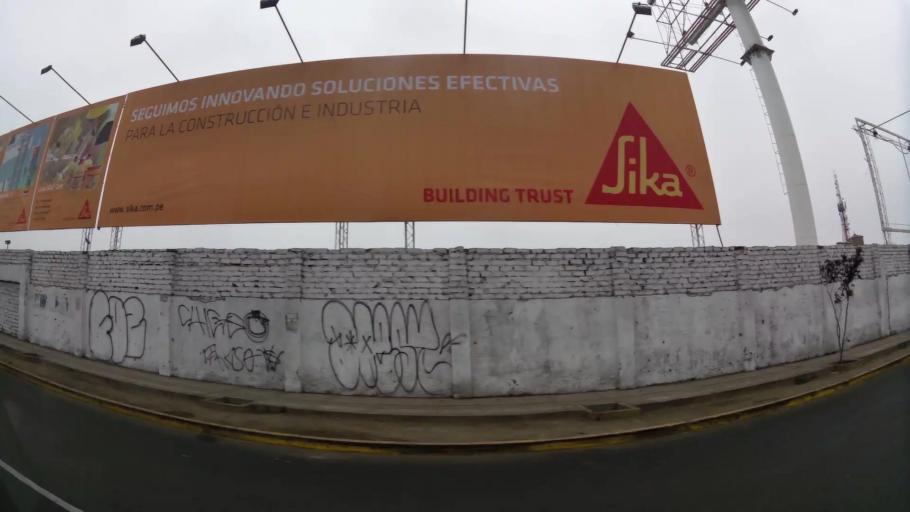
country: PE
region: Lima
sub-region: Lima
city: Surco
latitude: -12.1098
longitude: -77.0142
